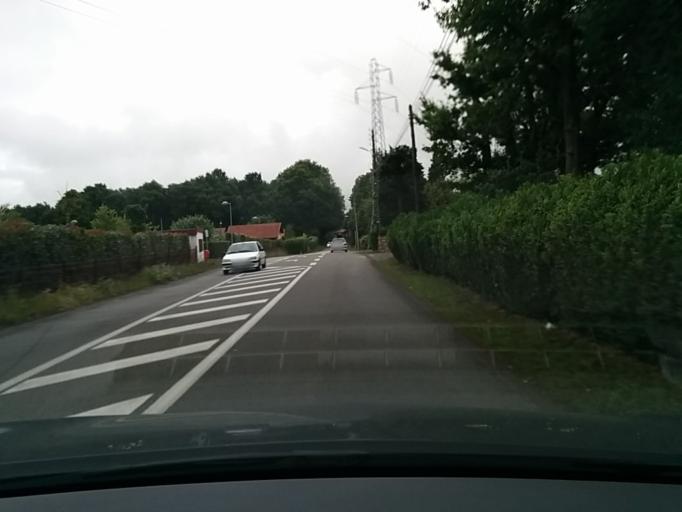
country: FR
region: Aquitaine
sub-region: Departement des Pyrenees-Atlantiques
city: Saint-Jean-de-Luz
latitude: 43.3922
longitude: -1.6350
